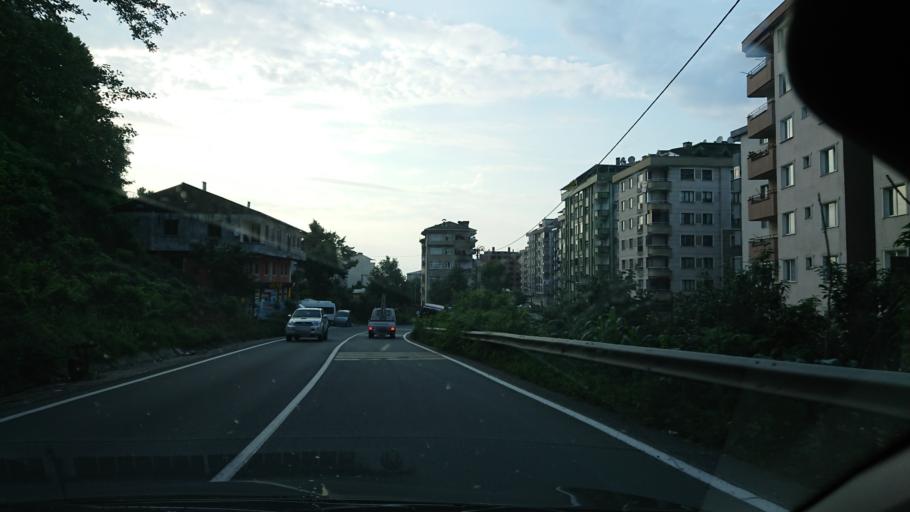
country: TR
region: Rize
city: Cayeli
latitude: 41.0796
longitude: 40.7131
